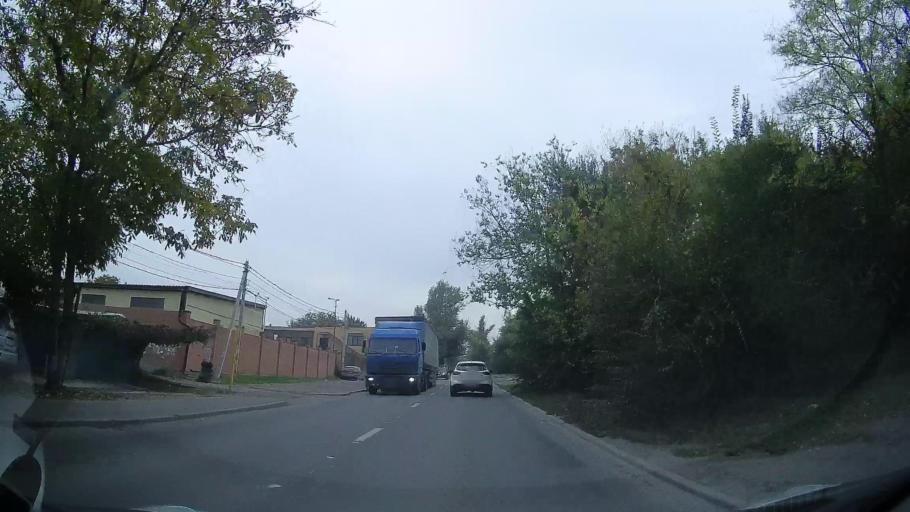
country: RU
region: Rostov
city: Severnyy
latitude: 47.2837
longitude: 39.6625
